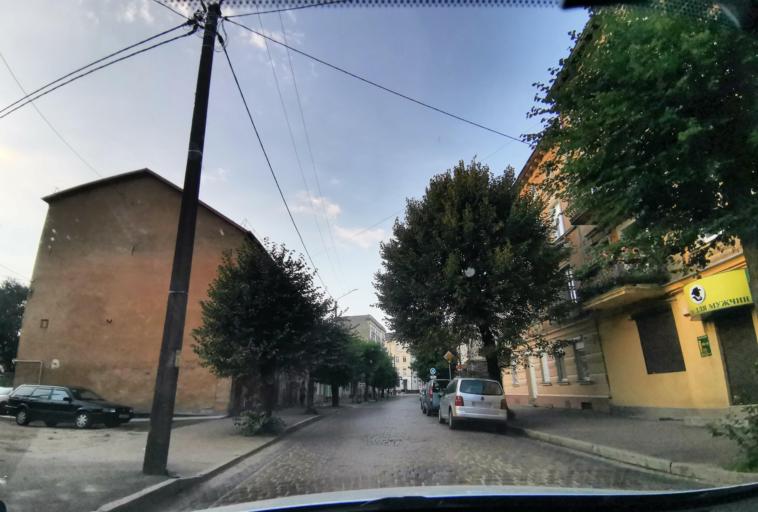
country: RU
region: Kaliningrad
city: Sovetsk
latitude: 55.0802
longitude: 21.8902
